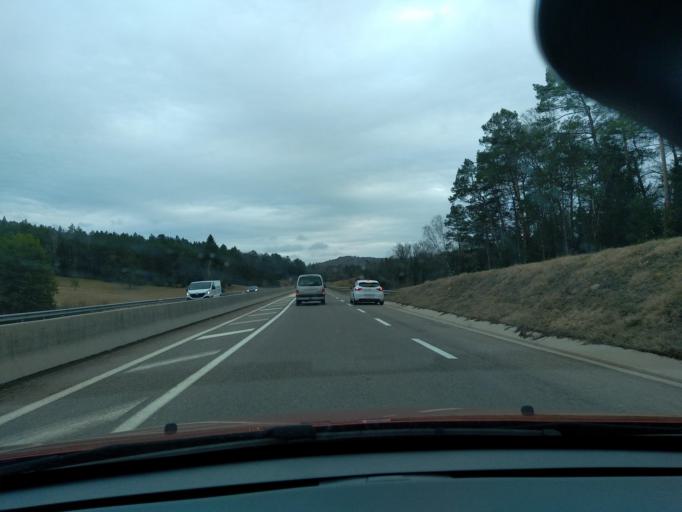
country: FR
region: Rhone-Alpes
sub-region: Departement de l'Ain
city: Dortan
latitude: 46.3131
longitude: 5.6693
